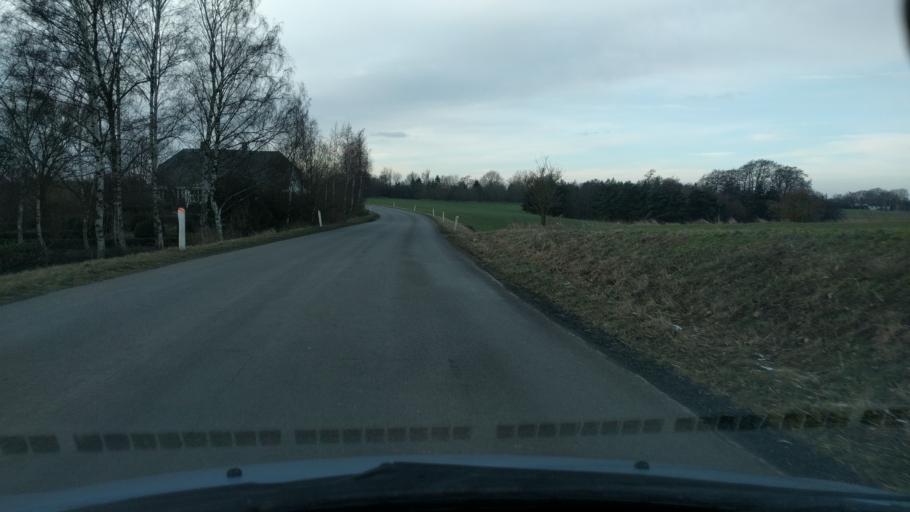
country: DK
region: Zealand
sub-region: Guldborgsund Kommune
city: Stubbekobing
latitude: 54.8603
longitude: 12.0247
